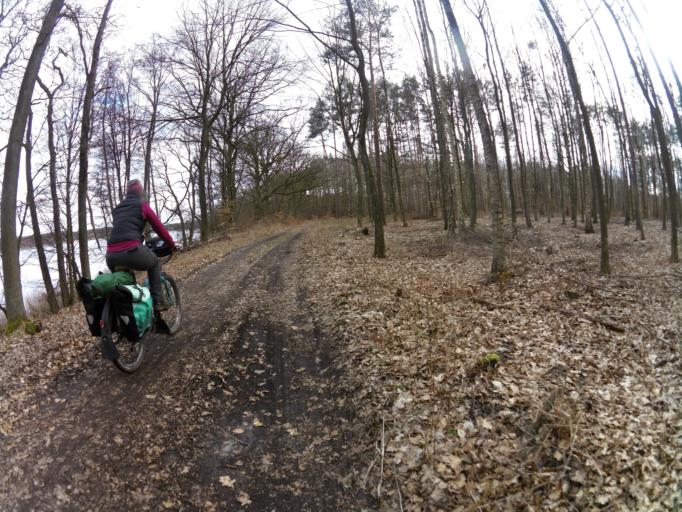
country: PL
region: Lubusz
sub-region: Powiat gorzowski
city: Lubiszyn
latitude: 52.7898
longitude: 14.8369
